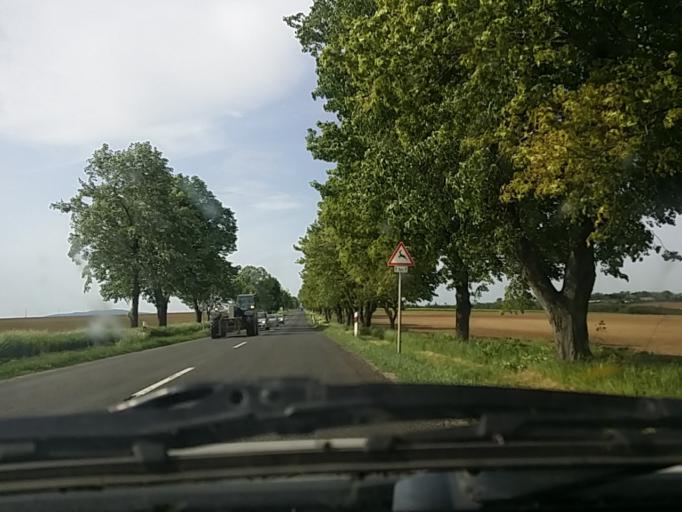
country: HU
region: Baranya
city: Kozarmisleny
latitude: 45.9694
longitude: 18.2312
